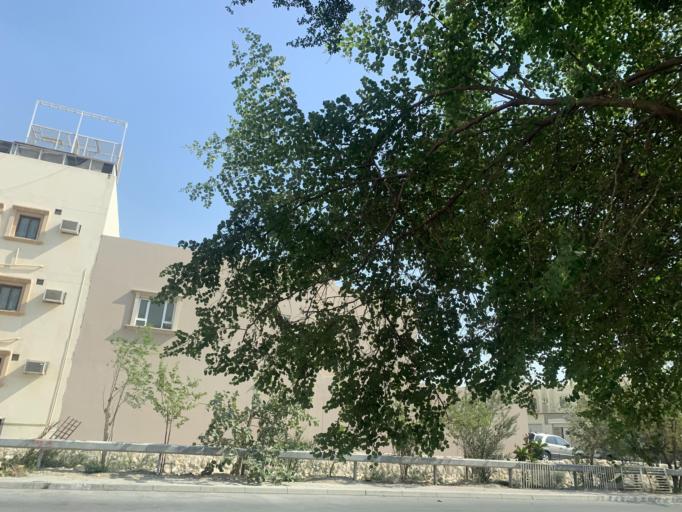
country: BH
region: Central Governorate
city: Madinat Hamad
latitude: 26.1261
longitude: 50.4901
